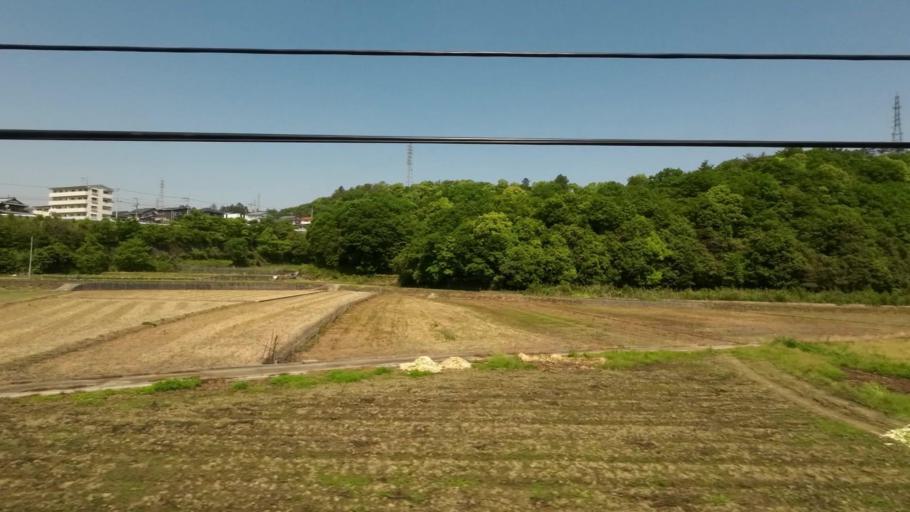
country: JP
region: Ehime
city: Niihama
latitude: 33.9325
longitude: 133.2720
